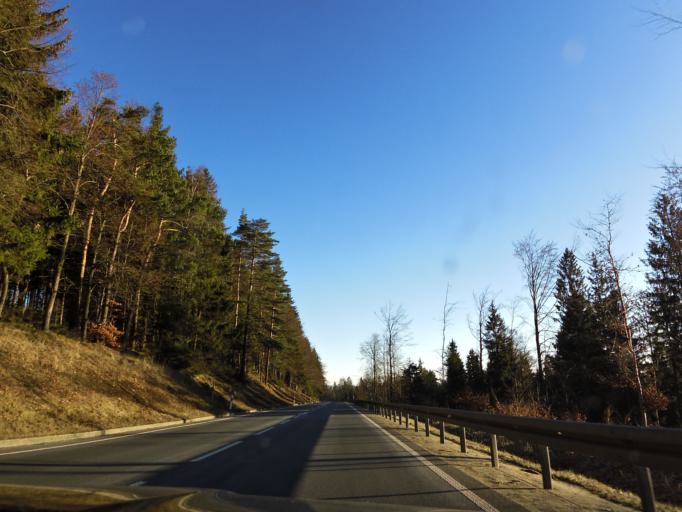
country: DE
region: Bavaria
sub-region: Upper Franconia
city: Fichtelberg
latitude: 50.0094
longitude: 11.8856
